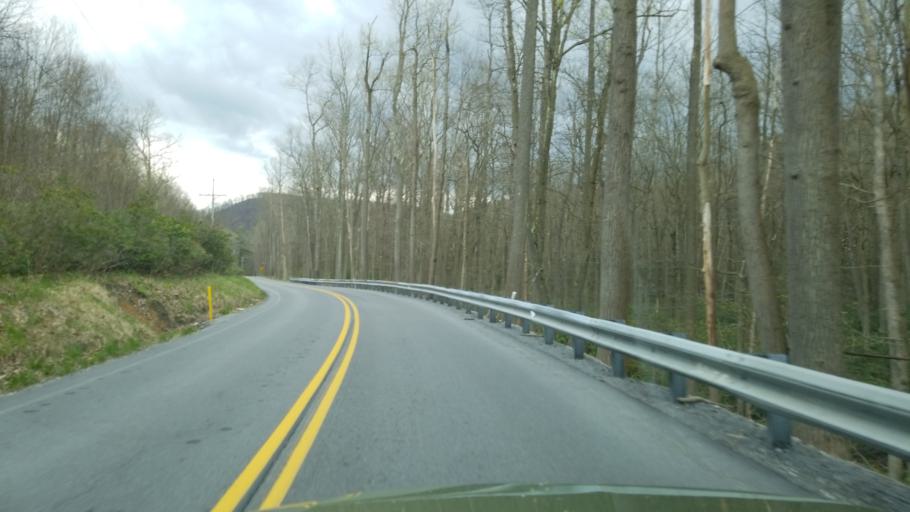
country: US
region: Pennsylvania
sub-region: Blair County
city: Tipton
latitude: 40.6655
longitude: -78.3322
